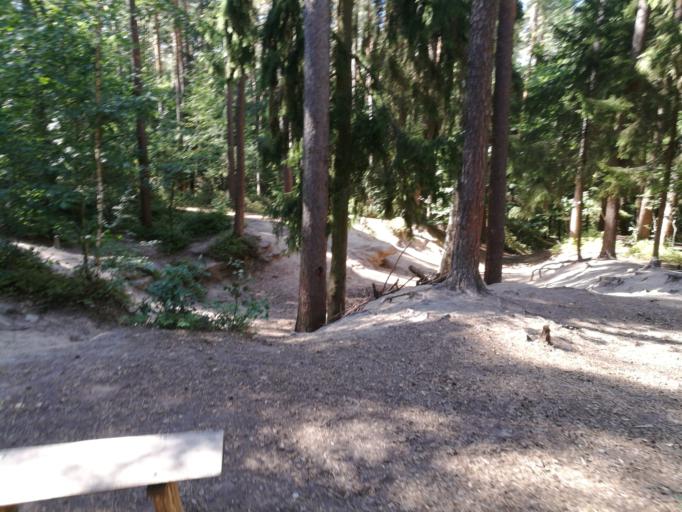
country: DE
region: Bavaria
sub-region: Regierungsbezirk Mittelfranken
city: Zirndorf
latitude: 49.4640
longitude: 10.9444
